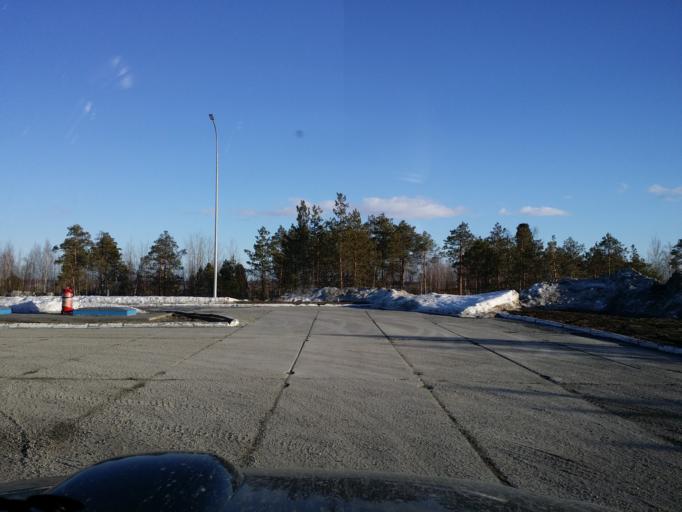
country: RU
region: Khanty-Mansiyskiy Avtonomnyy Okrug
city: Megion
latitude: 61.0653
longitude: 76.2116
